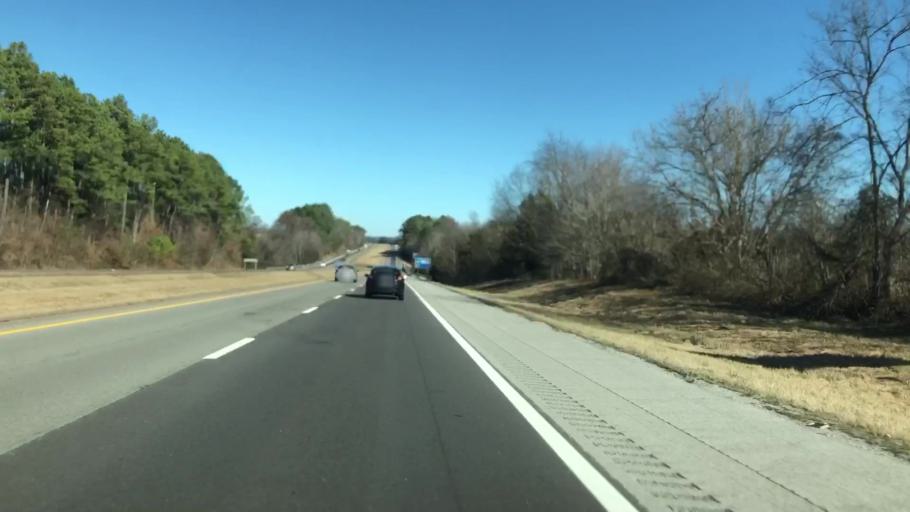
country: US
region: Tennessee
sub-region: Marshall County
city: Cornersville
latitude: 35.2872
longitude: -86.8848
